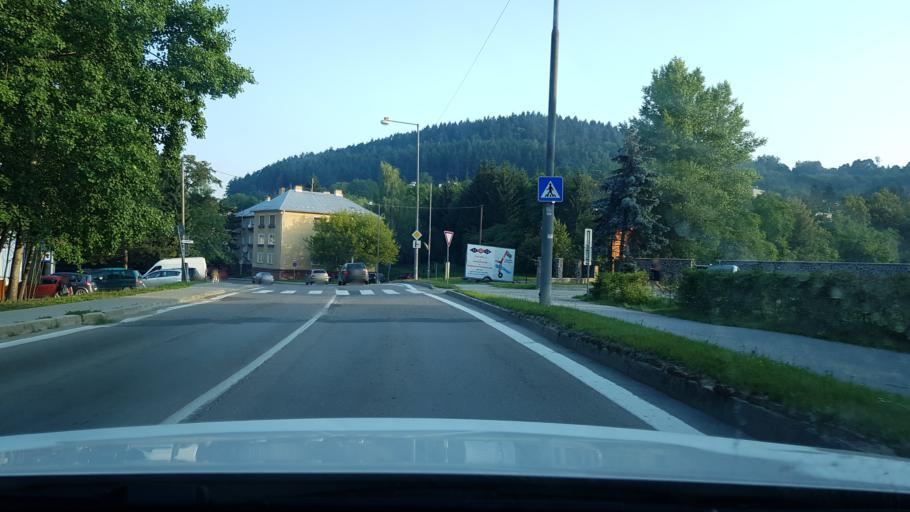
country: SK
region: Trenciansky
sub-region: Okres Povazska Bystrica
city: Povazska Bystrica
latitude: 49.1062
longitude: 18.4620
